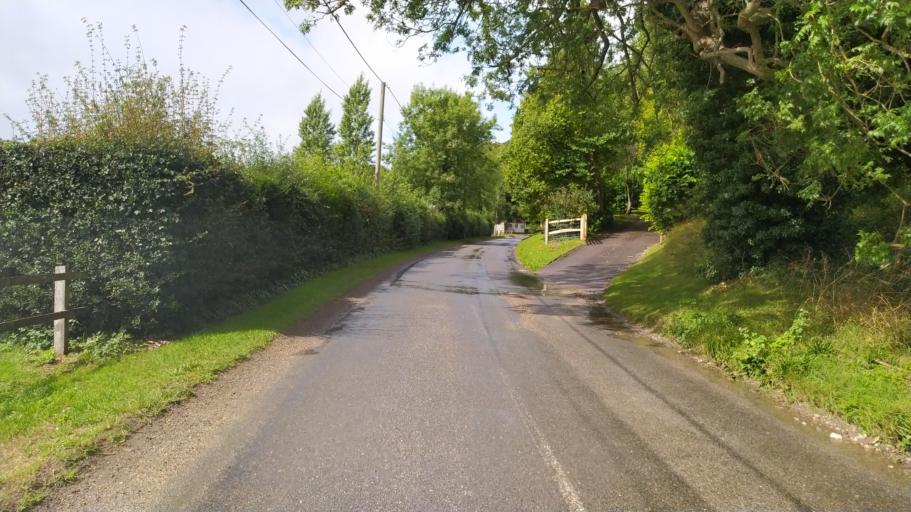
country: GB
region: England
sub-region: Hampshire
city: Swanmore
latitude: 51.0062
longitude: -1.1260
